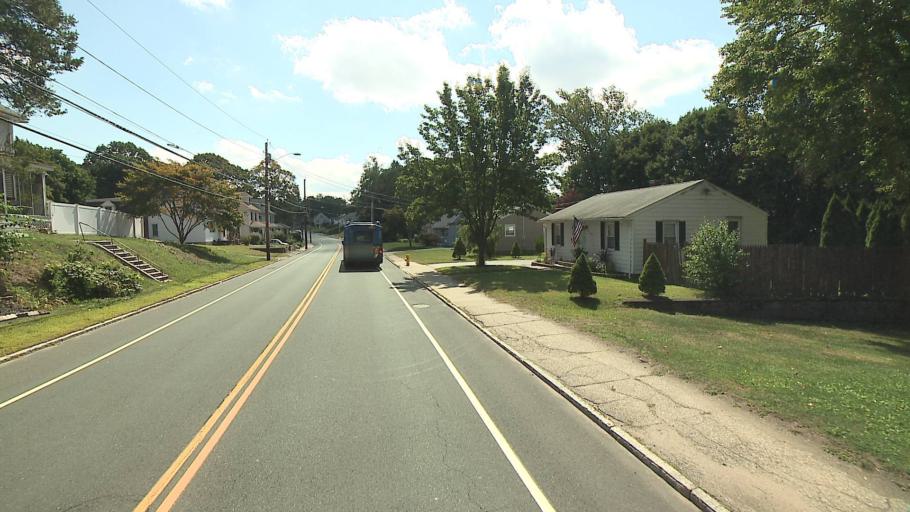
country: US
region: Connecticut
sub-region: New Haven County
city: Ansonia
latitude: 41.3615
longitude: -73.0831
